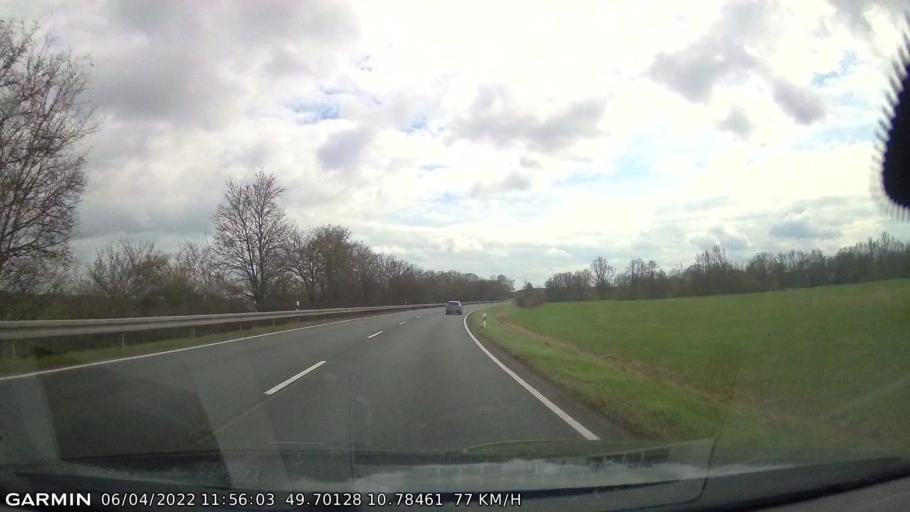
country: DE
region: Bavaria
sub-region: Regierungsbezirk Mittelfranken
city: Lonnerstadt
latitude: 49.7012
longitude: 10.7842
